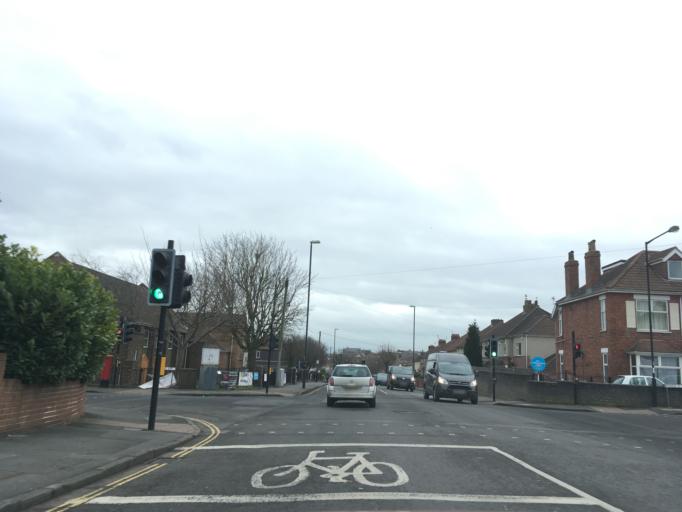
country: GB
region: England
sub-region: Bristol
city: Bristol
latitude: 51.4856
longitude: -2.5795
